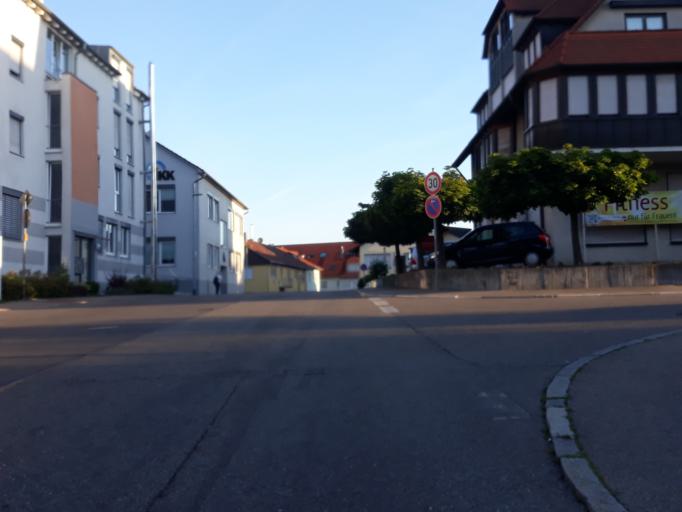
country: DE
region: Baden-Wuerttemberg
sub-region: Regierungsbezirk Stuttgart
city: Boeblingen
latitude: 48.6812
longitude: 9.0180
